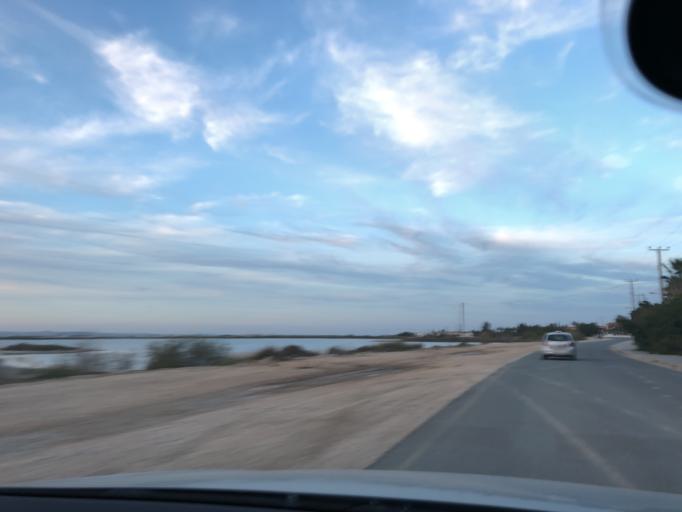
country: CY
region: Larnaka
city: Meneou
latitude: 34.8457
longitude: 33.6166
